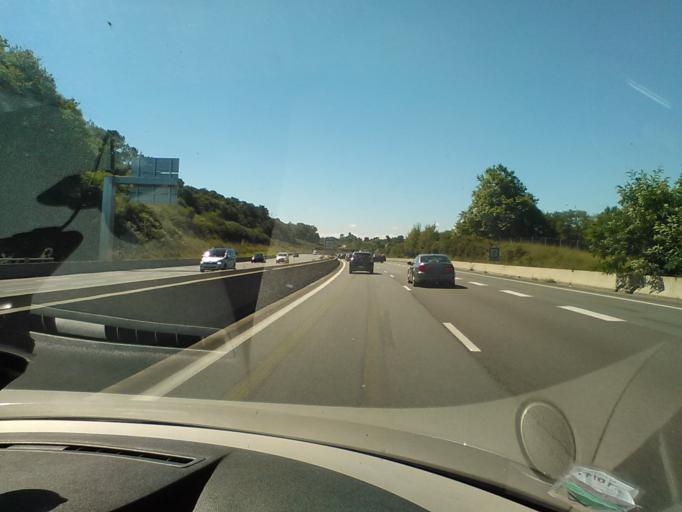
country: FR
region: Aquitaine
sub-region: Departement des Landes
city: Ondres
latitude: 43.5389
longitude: -1.4319
